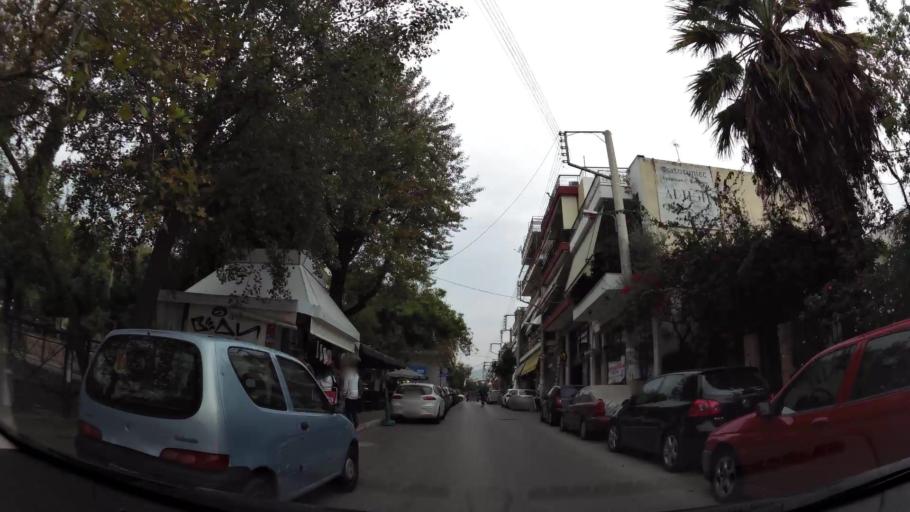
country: GR
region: Attica
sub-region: Nomarchia Athinas
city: Chaidari
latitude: 38.0048
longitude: 23.6759
